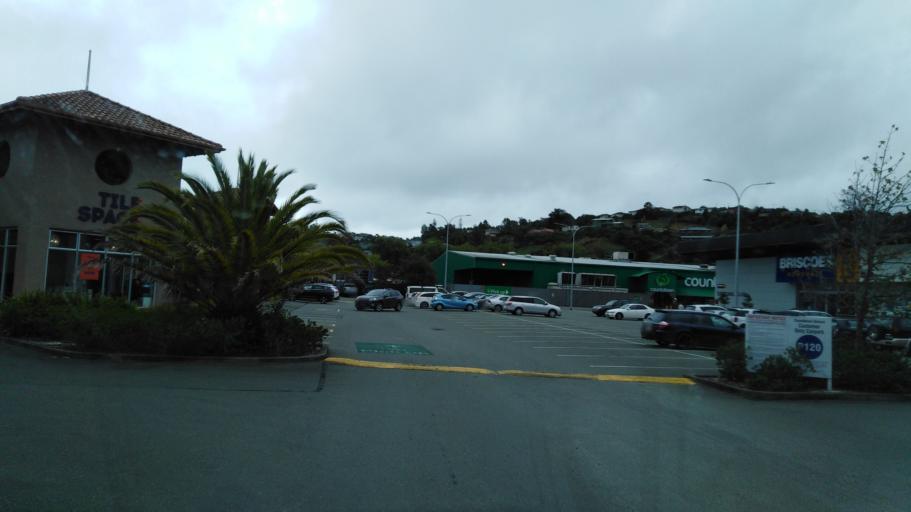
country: NZ
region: Nelson
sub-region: Nelson City
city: Nelson
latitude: -41.2739
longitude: 173.2785
